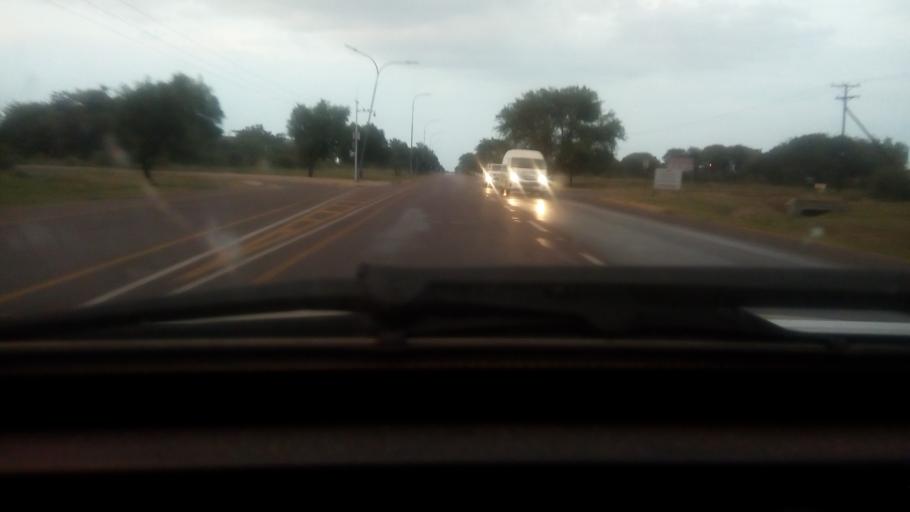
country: BW
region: Kweneng
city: Mmopone
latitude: -24.5919
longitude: 25.9184
